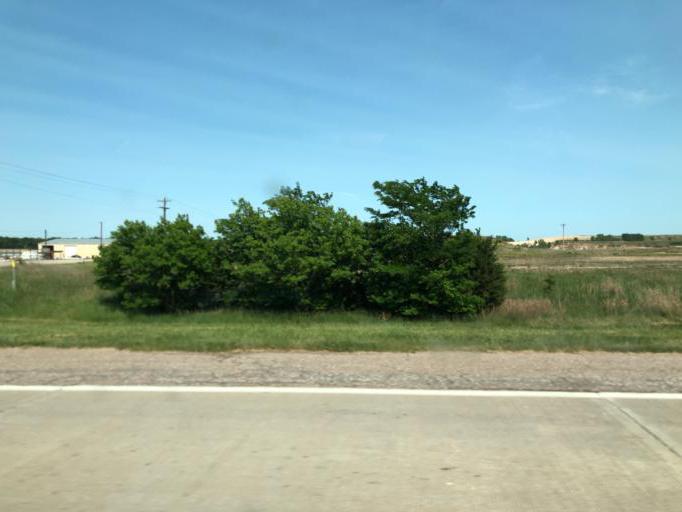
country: US
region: Nebraska
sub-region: Thayer County
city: Hebron
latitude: 40.2481
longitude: -97.5765
